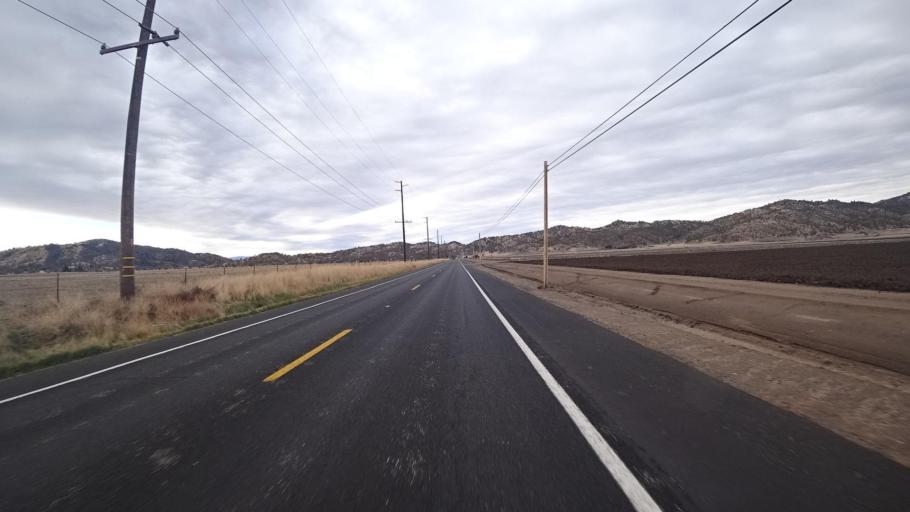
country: US
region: California
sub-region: Kern County
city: Stallion Springs
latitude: 35.0948
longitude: -118.6206
